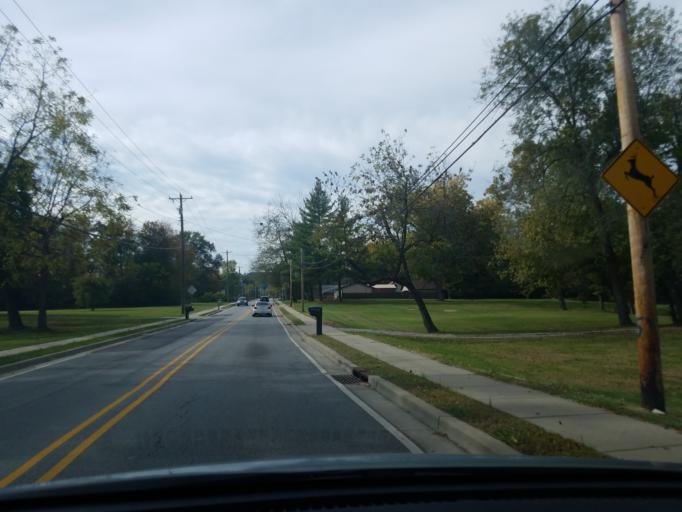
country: US
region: Indiana
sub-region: Floyd County
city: New Albany
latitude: 38.3102
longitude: -85.8327
